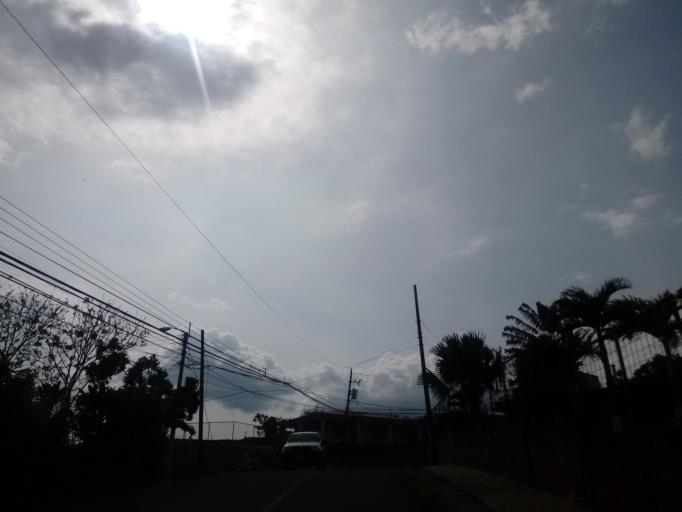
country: CR
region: Heredia
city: Angeles
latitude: 10.0234
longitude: -84.0474
